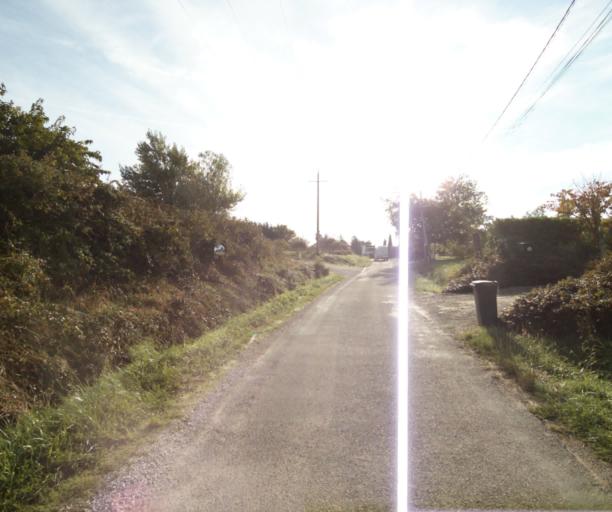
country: FR
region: Midi-Pyrenees
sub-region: Departement du Tarn-et-Garonne
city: Nohic
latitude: 43.9104
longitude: 1.4600
